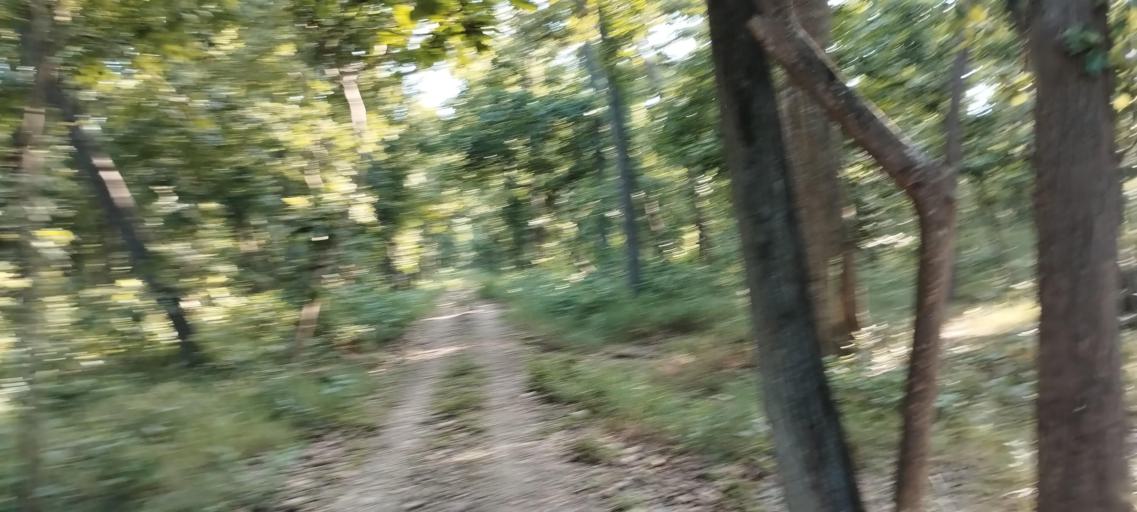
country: NP
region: Far Western
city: Tikapur
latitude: 28.5169
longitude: 81.2741
